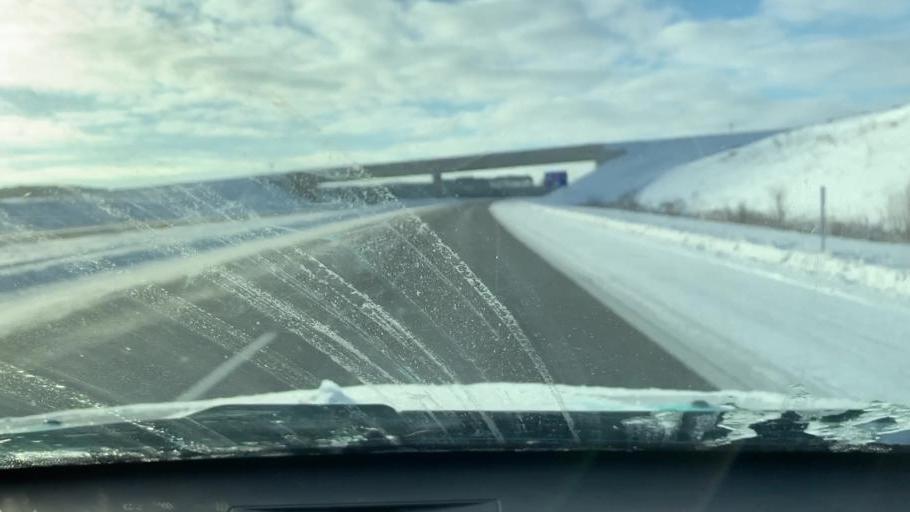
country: US
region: Michigan
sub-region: Wexford County
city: Cadillac
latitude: 44.3110
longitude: -85.3930
